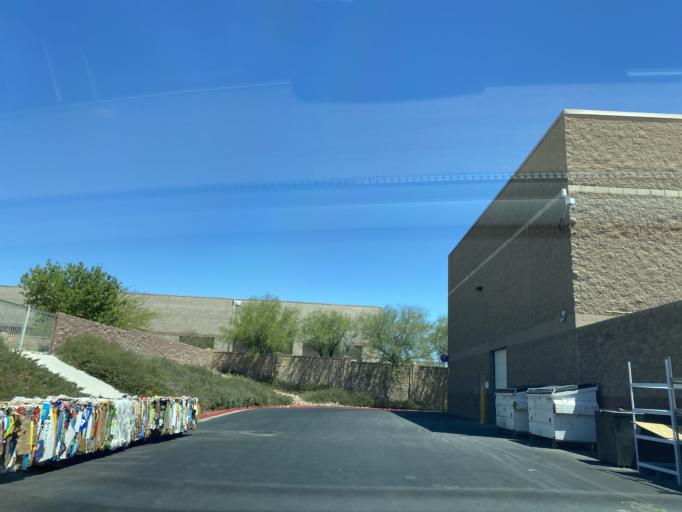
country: US
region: Nevada
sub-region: Clark County
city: Summerlin South
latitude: 36.2734
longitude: -115.2719
